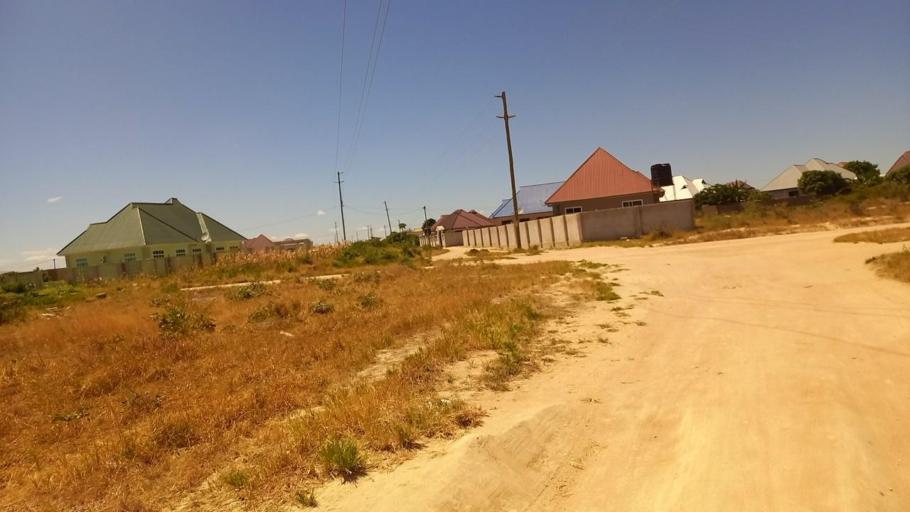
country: TZ
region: Dodoma
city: Dodoma
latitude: -6.1351
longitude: 35.7112
